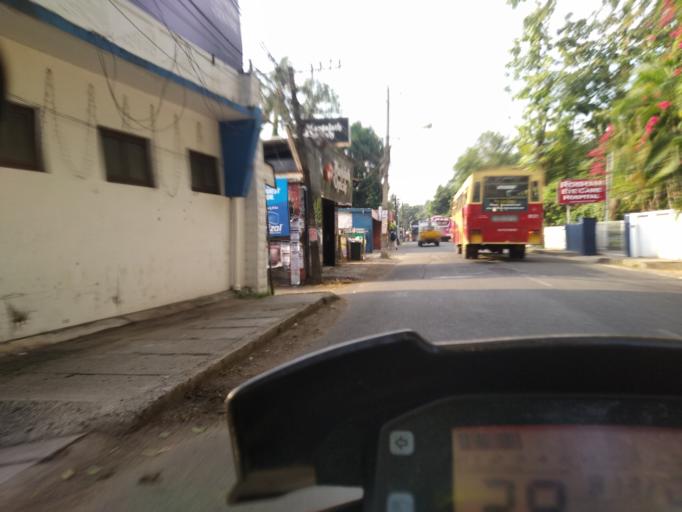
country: IN
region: Kerala
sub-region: Alappuzha
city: Arukutti
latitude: 9.9520
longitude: 76.3459
